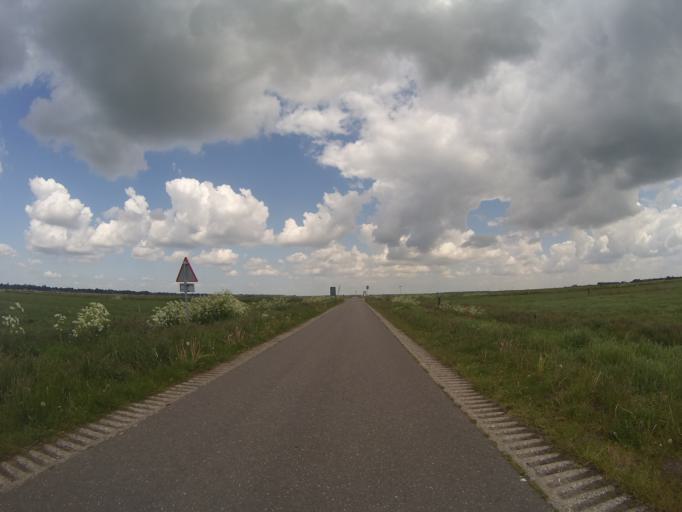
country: NL
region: Utrecht
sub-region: Gemeente Baarn
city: Baarn
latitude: 52.2441
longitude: 5.2866
